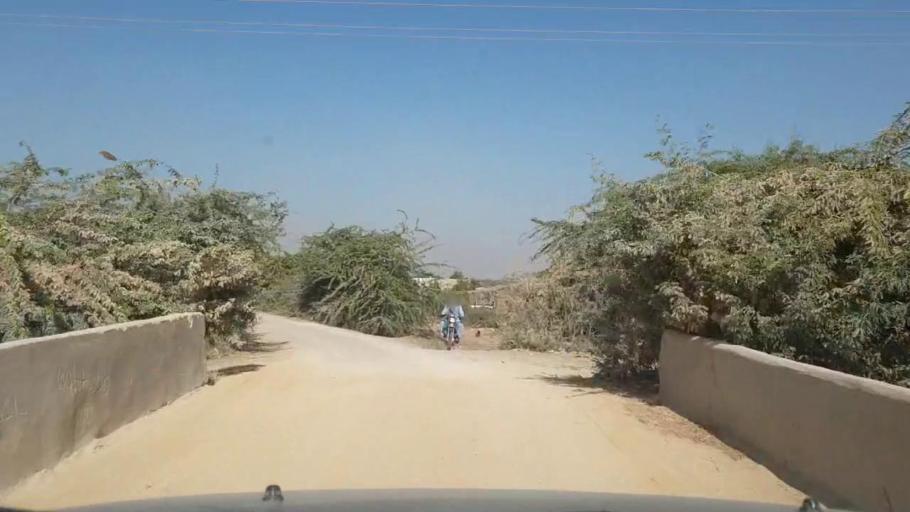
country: PK
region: Sindh
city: Thatta
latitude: 24.7853
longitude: 67.9084
